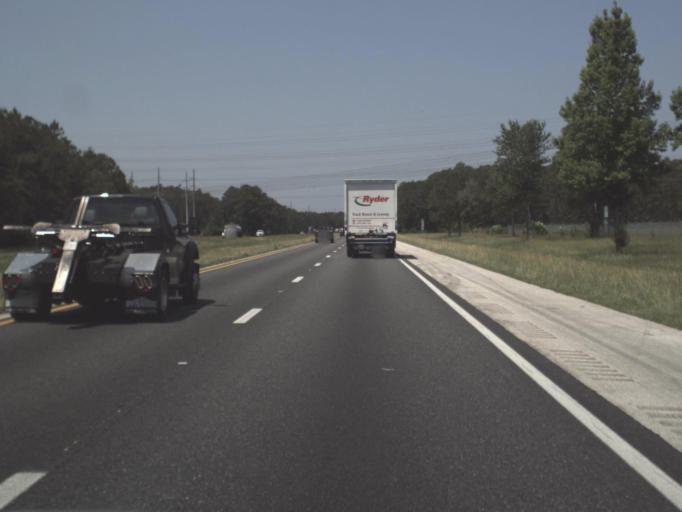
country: US
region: Florida
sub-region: Duval County
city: Baldwin
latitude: 30.2946
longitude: -81.9474
